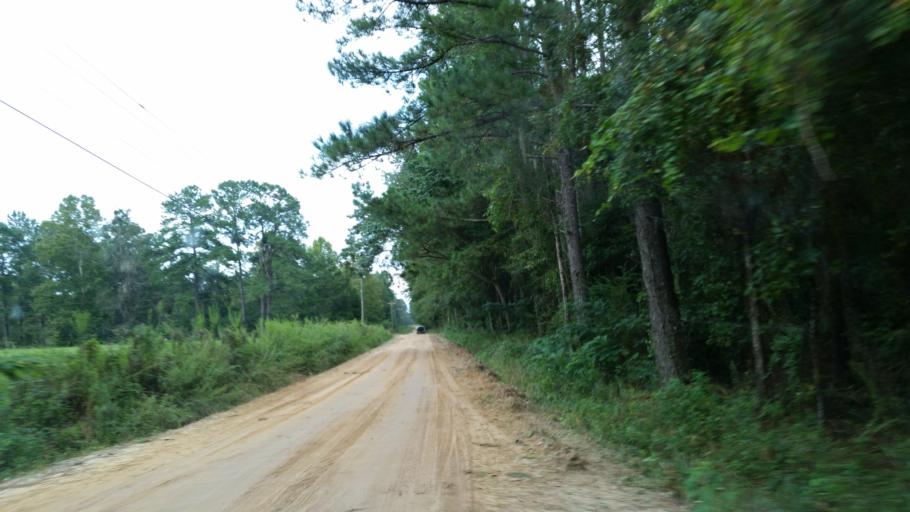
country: US
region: Georgia
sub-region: Lowndes County
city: Valdosta
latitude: 30.7214
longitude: -83.3072
